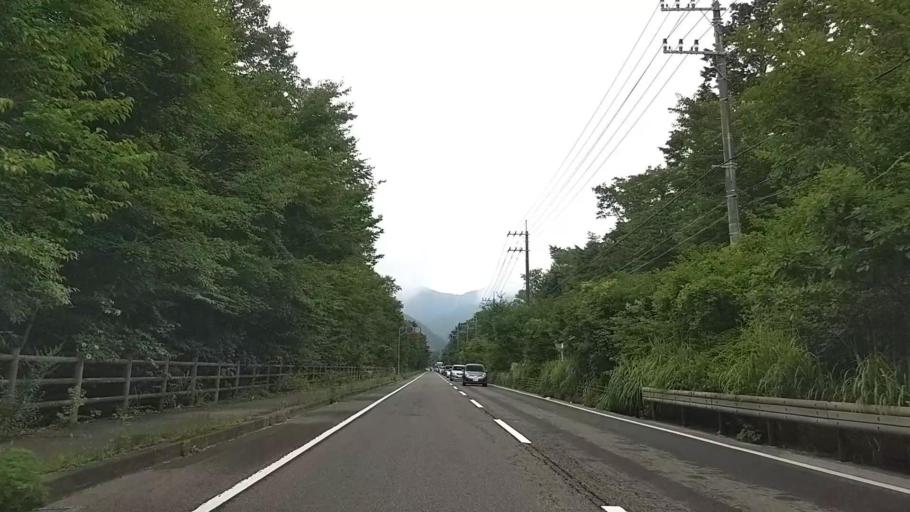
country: JP
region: Yamanashi
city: Fujikawaguchiko
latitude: 35.4841
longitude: 138.6508
